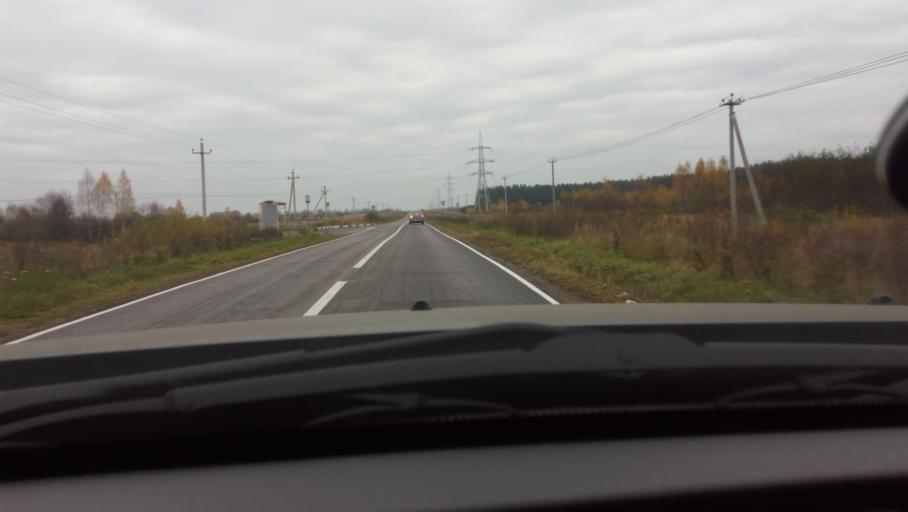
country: RU
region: Moskovskaya
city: Avsyunino
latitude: 55.6026
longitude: 39.1643
